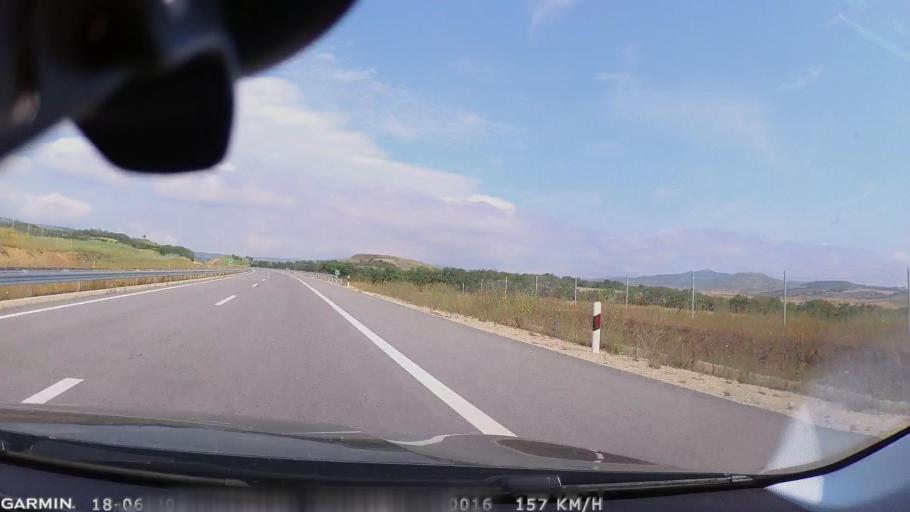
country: MK
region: Sveti Nikole
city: Gorobinci
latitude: 41.9116
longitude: 21.8981
